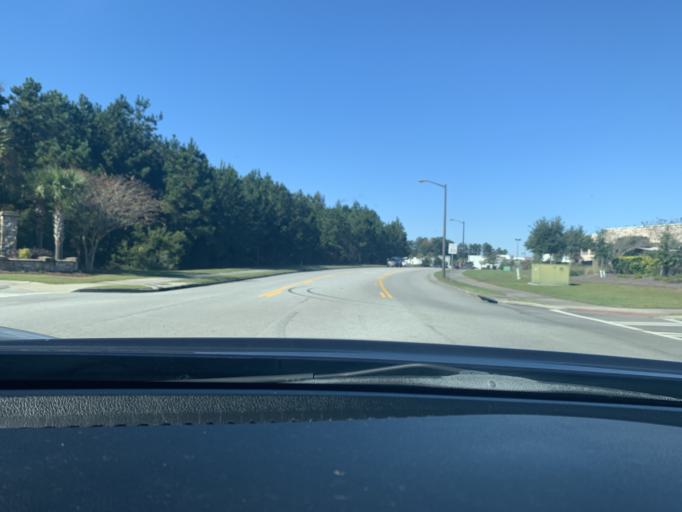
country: US
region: Georgia
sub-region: Chatham County
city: Pooler
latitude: 32.1327
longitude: -81.2501
